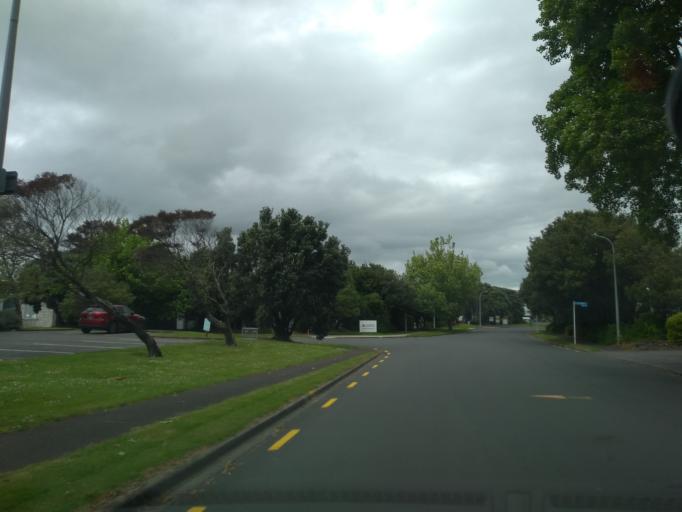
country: NZ
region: Auckland
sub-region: Auckland
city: Mangere
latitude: -36.9227
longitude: 174.8223
